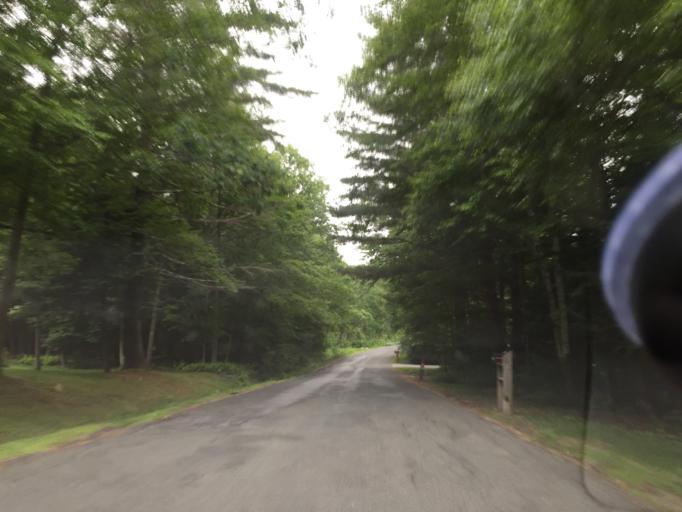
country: US
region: Connecticut
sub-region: Litchfield County
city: Litchfield
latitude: 41.8156
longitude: -73.2584
